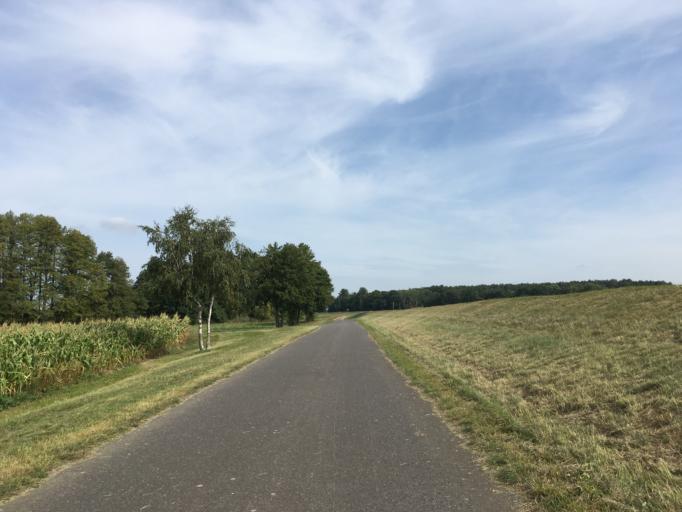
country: DE
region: Brandenburg
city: Schenkendobern
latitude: 51.8725
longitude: 14.6458
